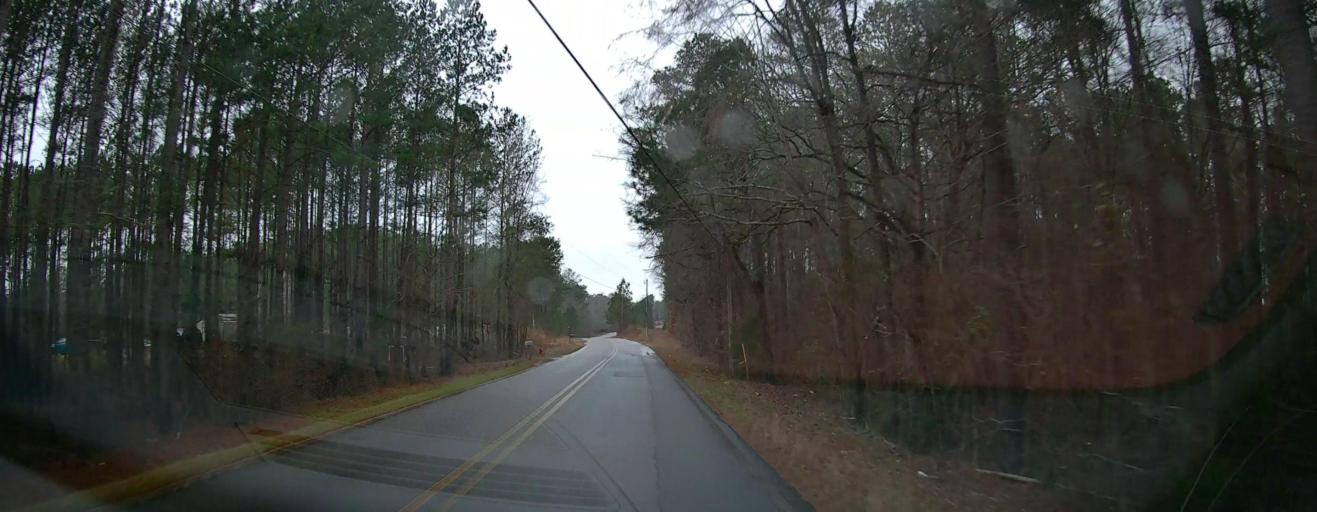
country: US
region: Georgia
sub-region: Monroe County
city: Forsyth
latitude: 33.0870
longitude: -83.9240
